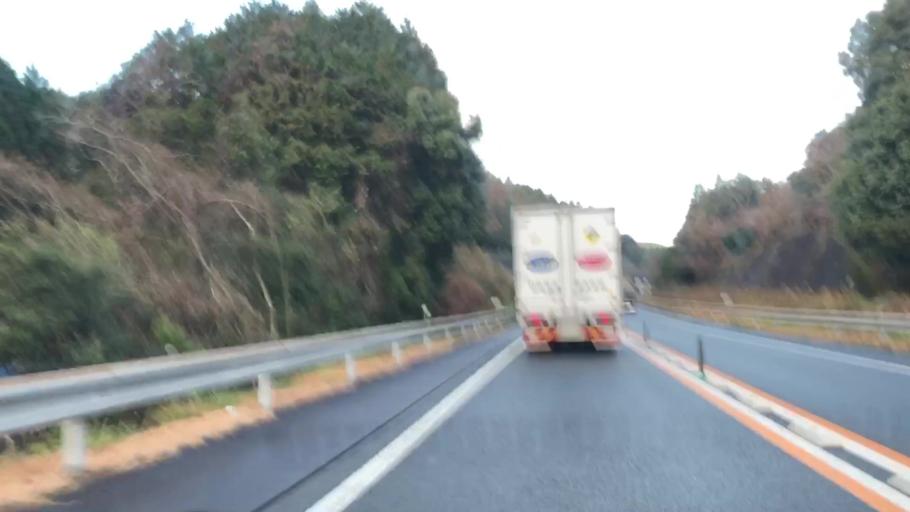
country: JP
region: Saga Prefecture
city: Imaricho-ko
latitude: 33.1557
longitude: 129.8769
